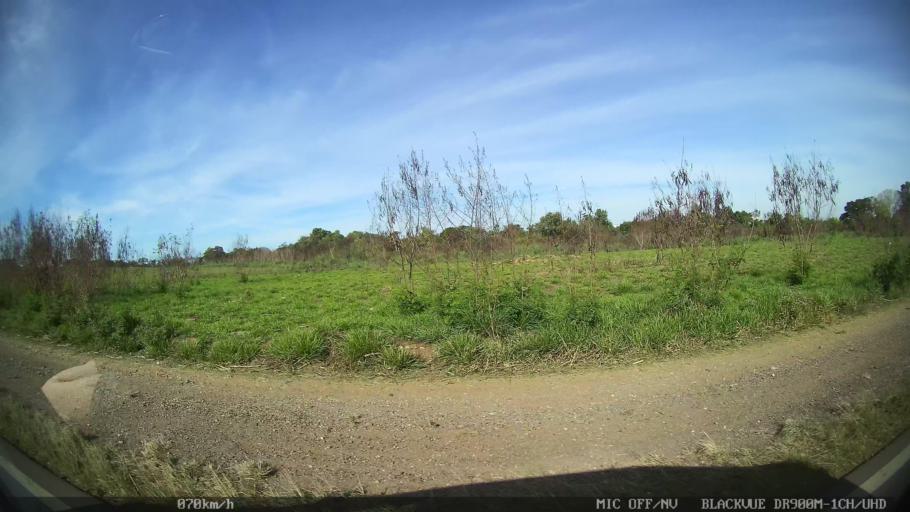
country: BR
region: Sao Paulo
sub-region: Rio Das Pedras
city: Rio das Pedras
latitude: -22.7924
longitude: -47.6231
